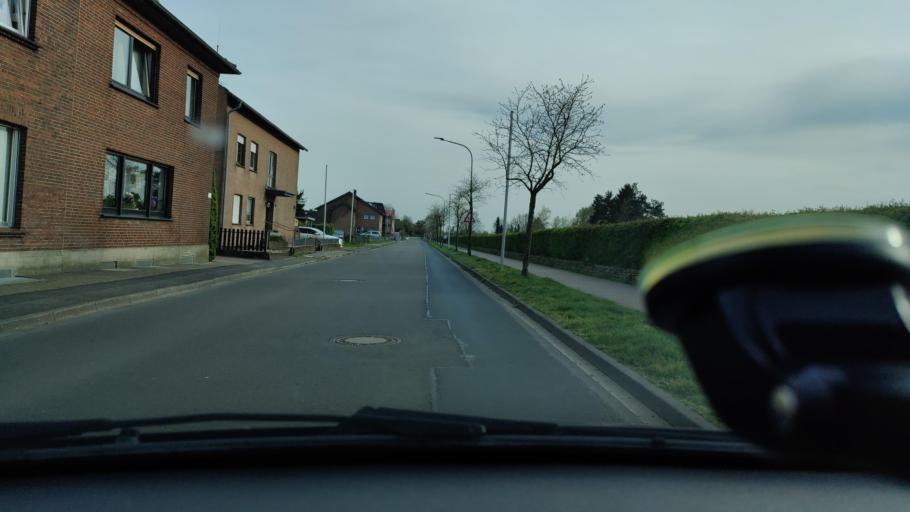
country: DE
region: North Rhine-Westphalia
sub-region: Regierungsbezirk Dusseldorf
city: Goch
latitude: 51.7173
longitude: 6.1656
